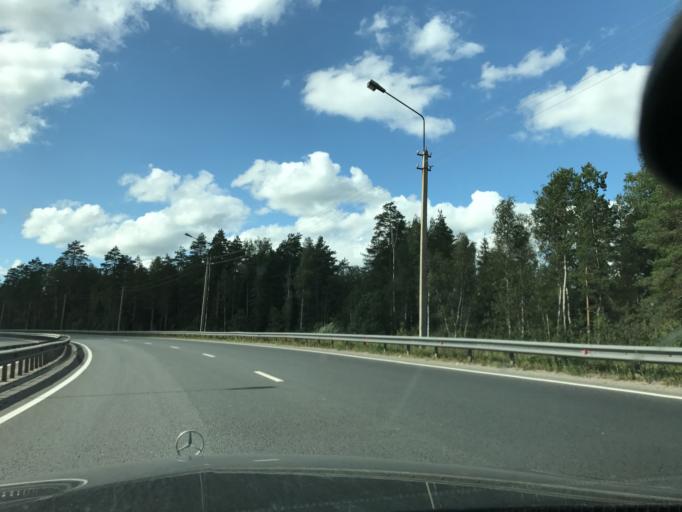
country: RU
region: Vladimir
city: Kameshkovo
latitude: 56.1971
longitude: 40.9592
